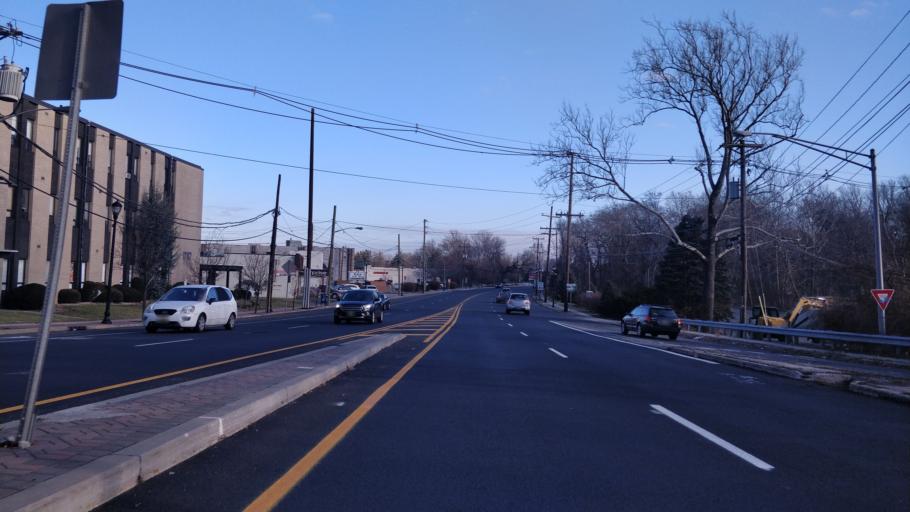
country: US
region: New Jersey
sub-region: Union County
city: Union
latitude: 40.6941
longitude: -74.2599
